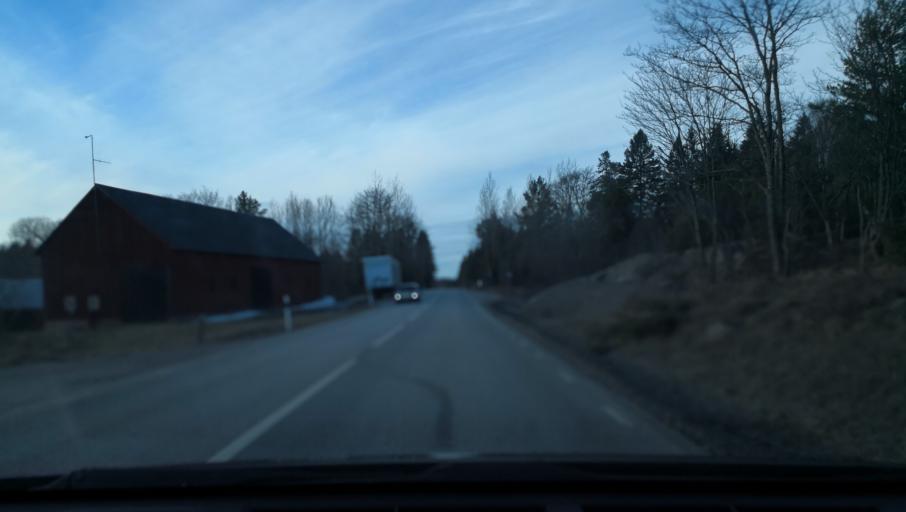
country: SE
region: Uppsala
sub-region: Osthammars Kommun
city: Gimo
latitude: 60.3390
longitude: 18.2164
